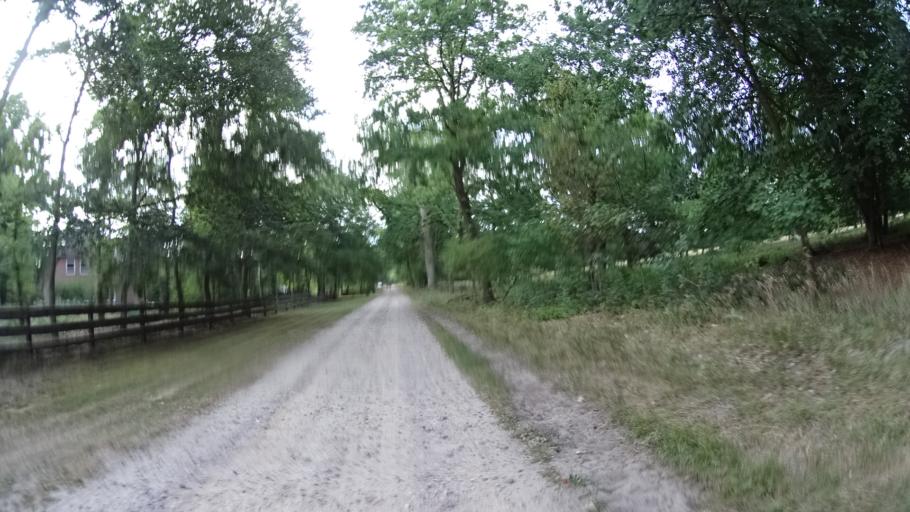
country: DE
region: Lower Saxony
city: Handeloh
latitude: 53.2143
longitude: 9.8807
